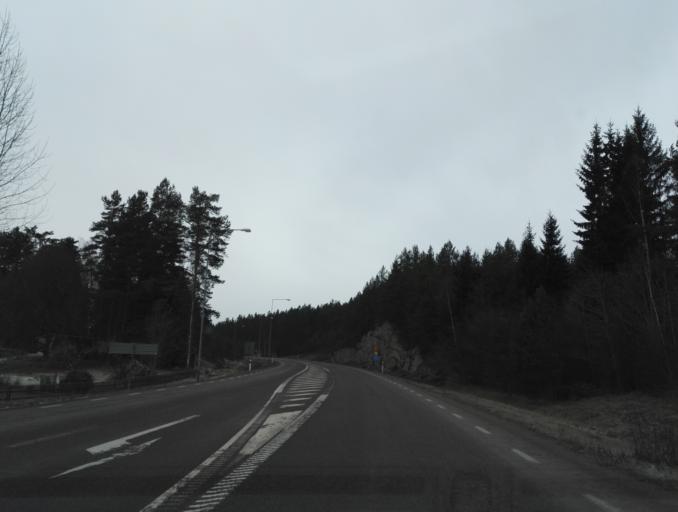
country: SE
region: Kalmar
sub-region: Hultsfreds Kommun
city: Virserum
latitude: 57.3437
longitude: 15.6061
